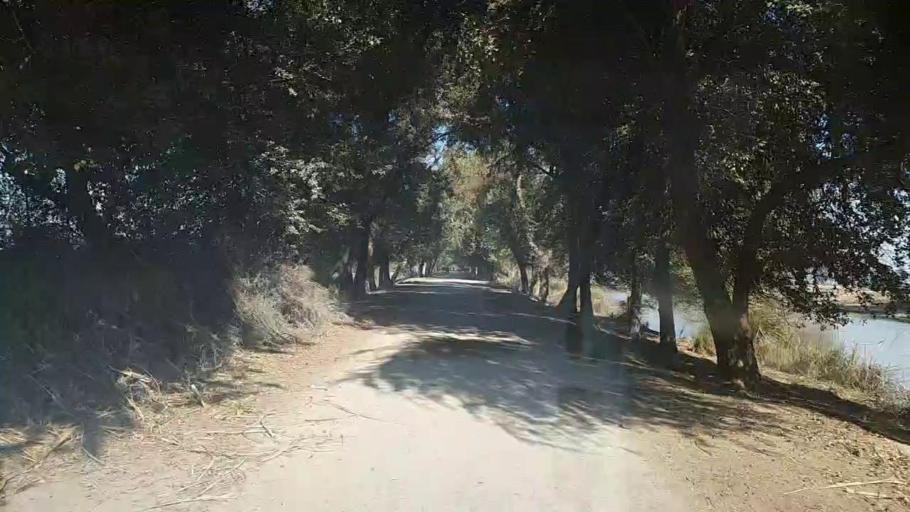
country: PK
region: Sindh
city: Khairpur
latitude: 28.0006
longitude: 69.6521
